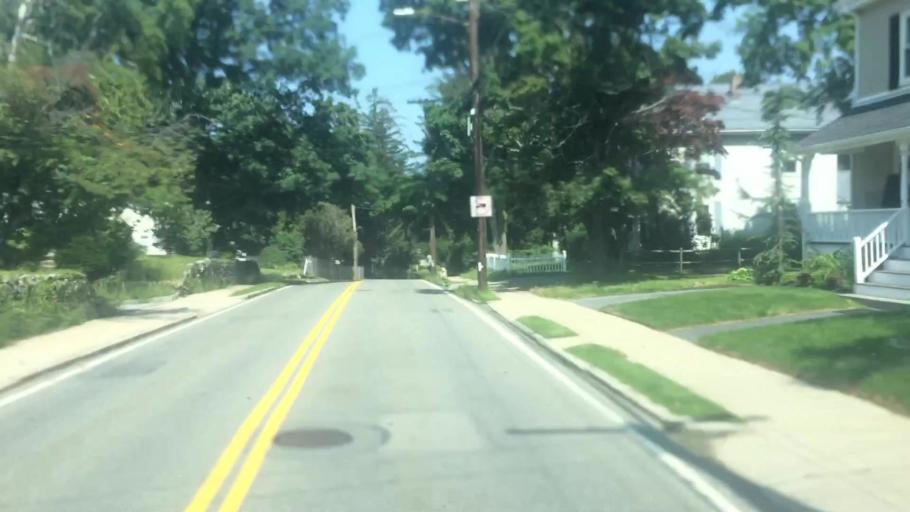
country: US
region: Massachusetts
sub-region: Middlesex County
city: Woburn
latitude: 42.4924
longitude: -71.1498
